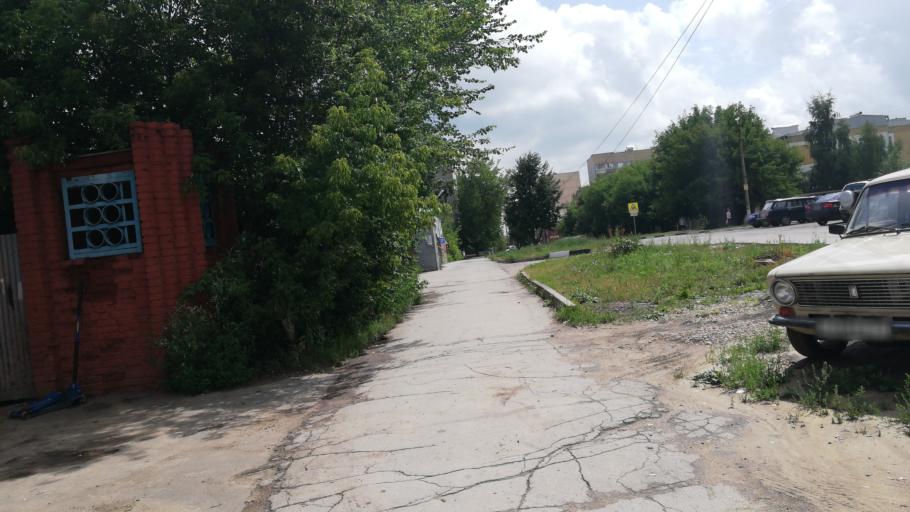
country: RU
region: Tula
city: Tula
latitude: 54.1993
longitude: 37.6407
